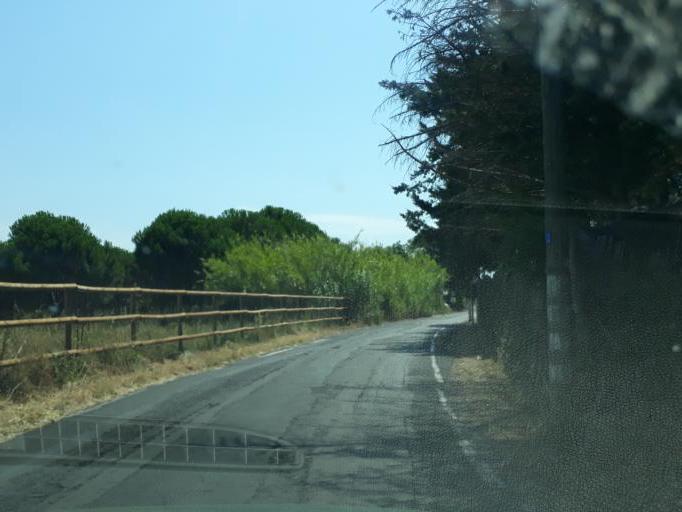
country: FR
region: Languedoc-Roussillon
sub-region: Departement de l'Herault
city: Agde
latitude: 43.2855
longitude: 3.4829
